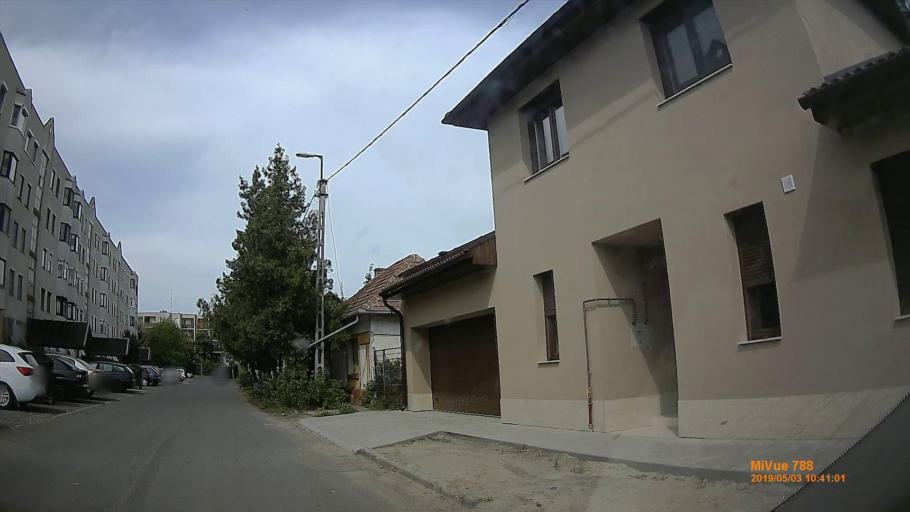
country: HU
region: Jasz-Nagykun-Szolnok
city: Szolnok
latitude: 47.1833
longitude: 20.1942
